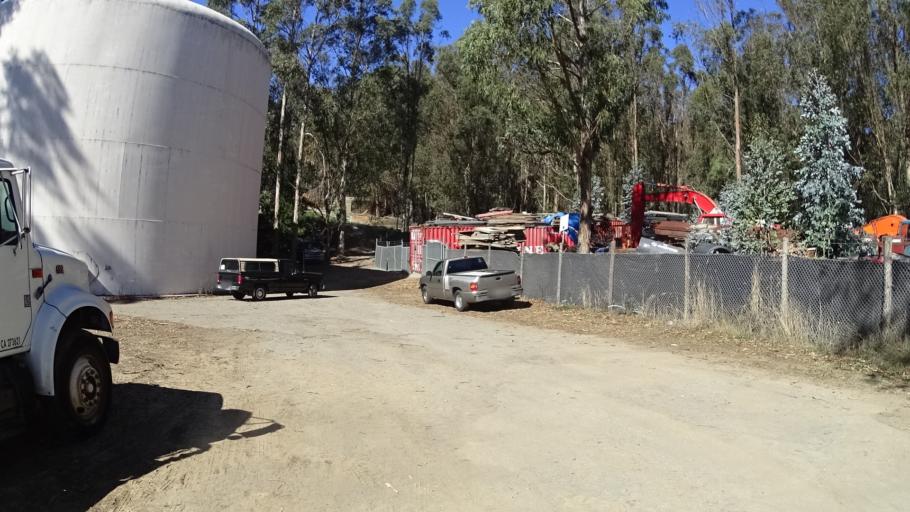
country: US
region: California
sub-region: San Mateo County
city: Colma
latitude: 37.6767
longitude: -122.4377
